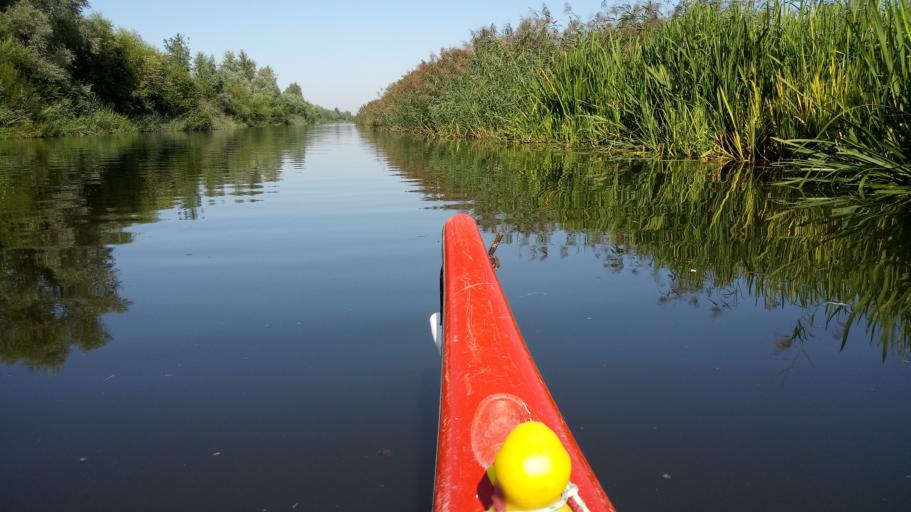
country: NL
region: Overijssel
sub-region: Gemeente Haaksbergen
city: Haaksbergen
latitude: 52.0945
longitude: 6.7163
